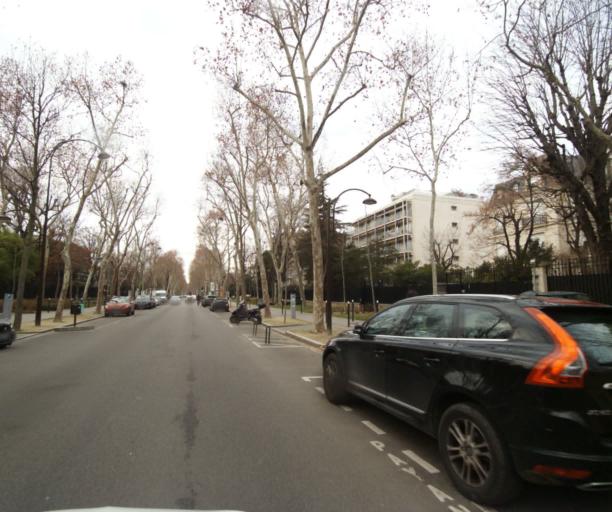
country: FR
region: Ile-de-France
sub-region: Departement des Hauts-de-Seine
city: Neuilly-sur-Seine
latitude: 48.8912
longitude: 2.2717
